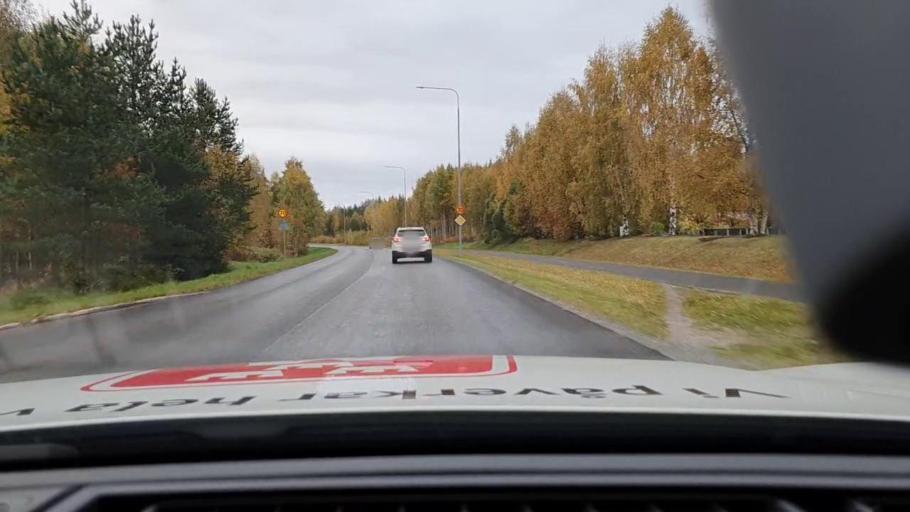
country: SE
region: Norrbotten
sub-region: Bodens Kommun
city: Saevast
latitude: 65.7616
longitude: 21.7389
